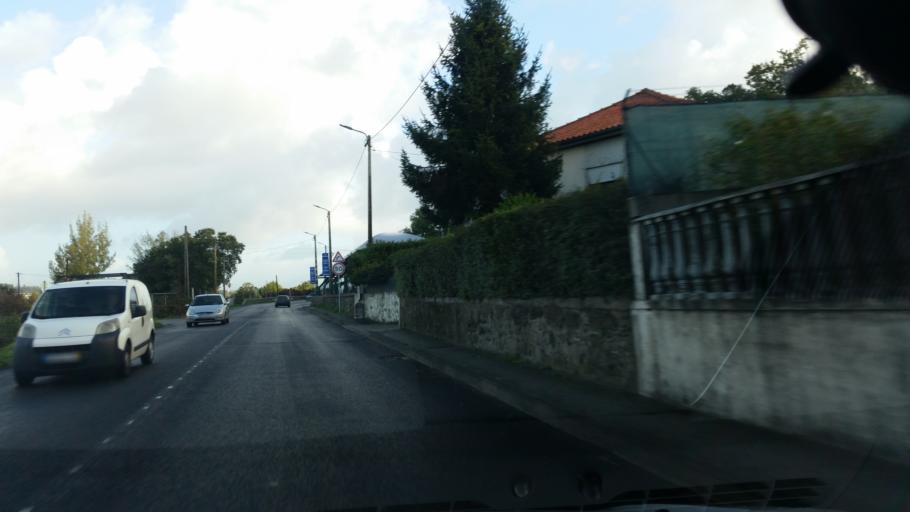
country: PT
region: Porto
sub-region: Santo Tirso
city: Sao Miguel do Couto
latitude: 41.3461
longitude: -8.4625
